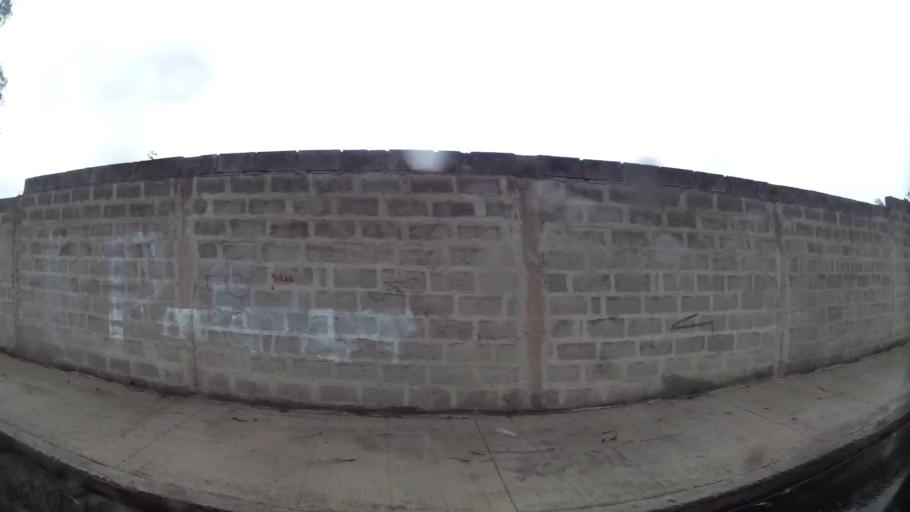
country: EC
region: Pichincha
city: Sangolqui
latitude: -0.3006
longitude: -78.4506
